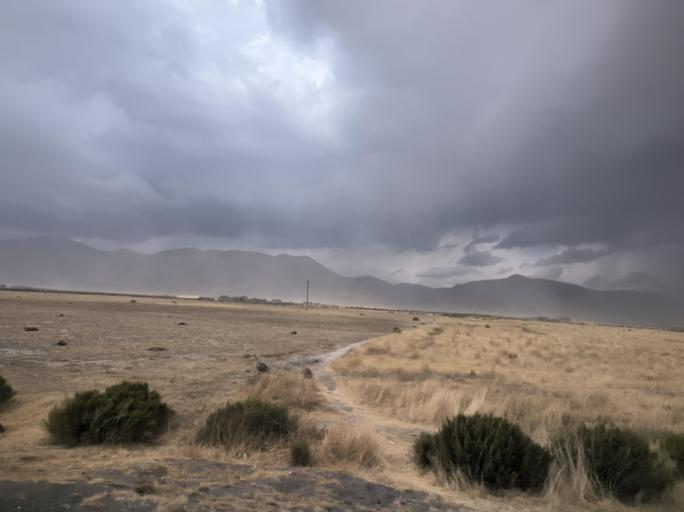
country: BO
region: Oruro
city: Challapata
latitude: -18.7762
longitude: -66.8531
